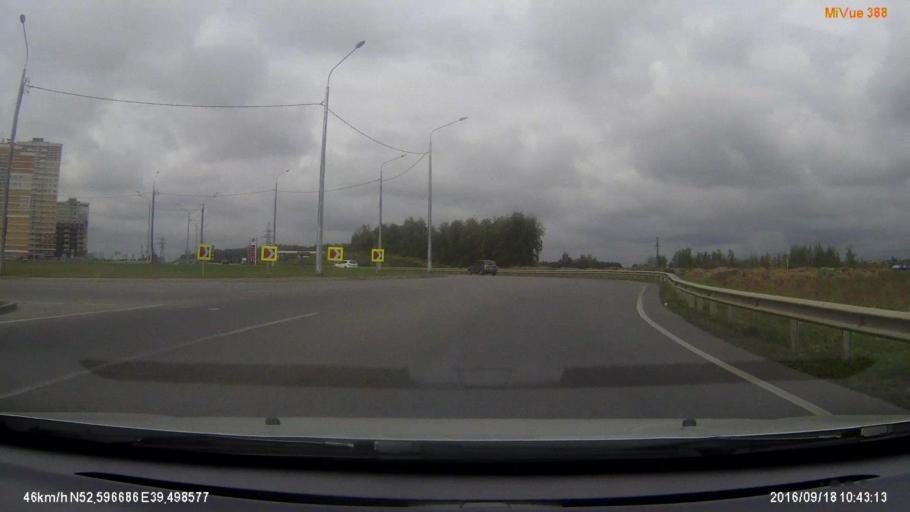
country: RU
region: Lipetsk
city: Syrskoye
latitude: 52.5966
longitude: 39.4988
